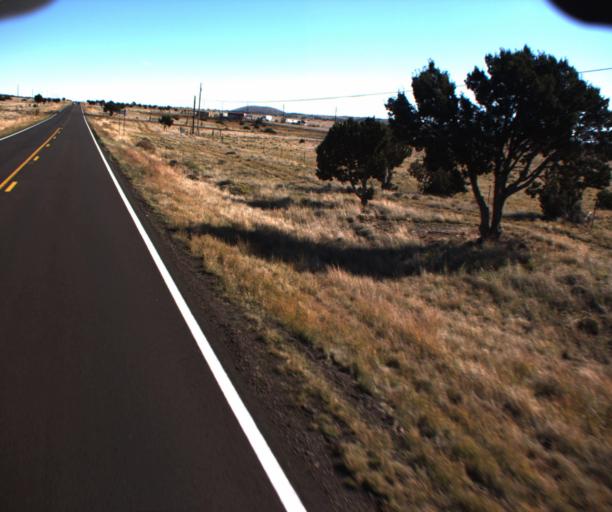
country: US
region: Arizona
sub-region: Navajo County
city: White Mountain Lake
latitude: 34.3895
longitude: -109.6701
